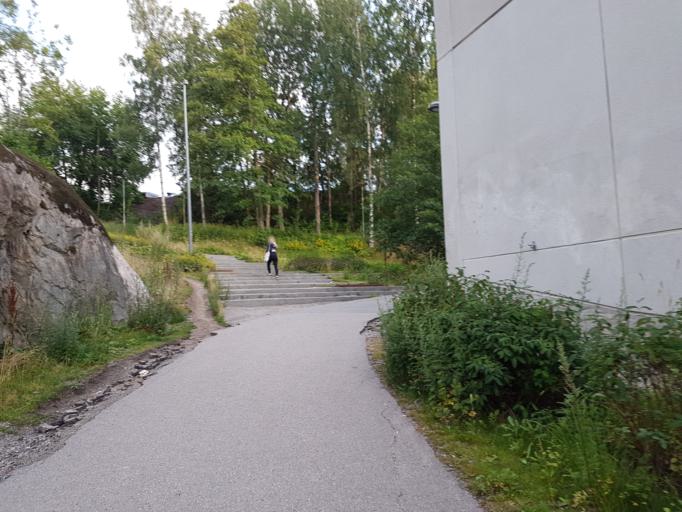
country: SE
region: Stockholm
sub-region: Huddinge Kommun
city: Huddinge
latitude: 59.2168
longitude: 17.9482
